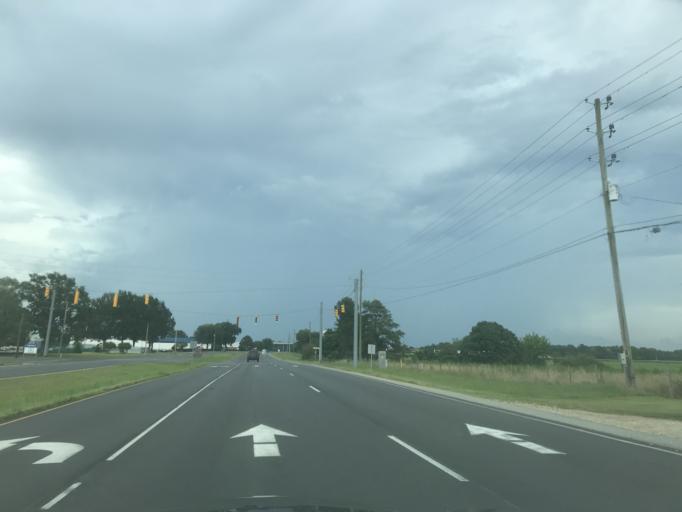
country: US
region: North Carolina
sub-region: Johnston County
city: Clayton
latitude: 35.6241
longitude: -78.4251
